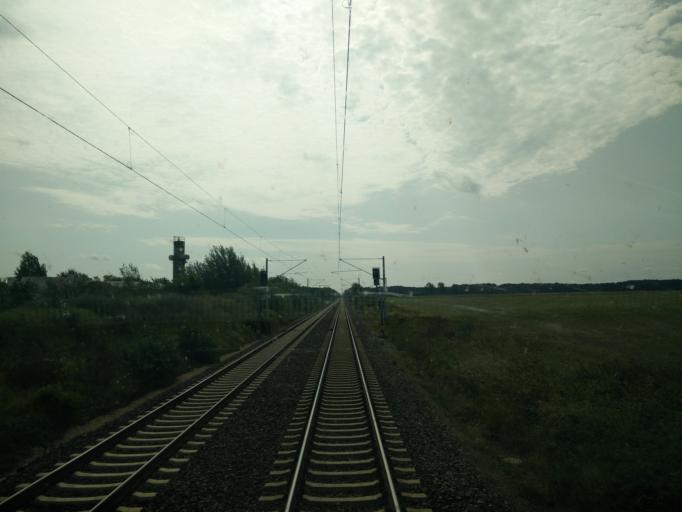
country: DE
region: Brandenburg
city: Luebben
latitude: 51.9236
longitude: 13.8932
